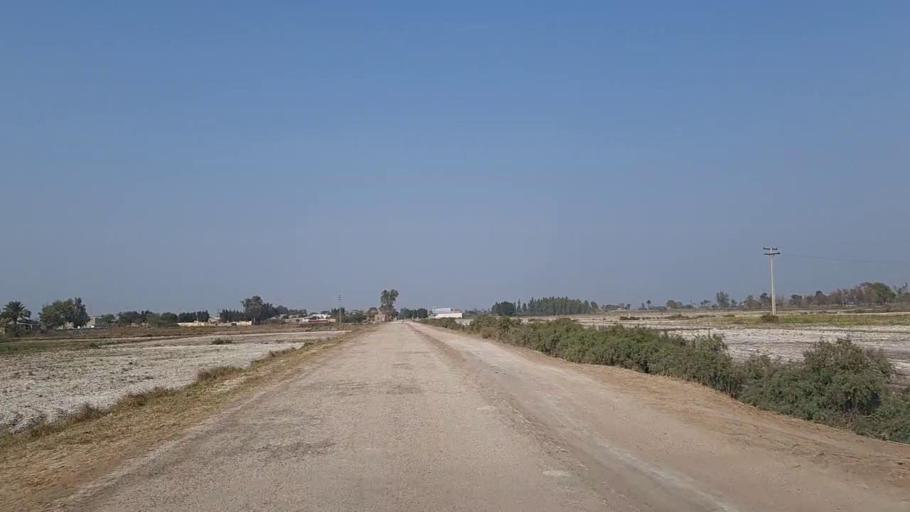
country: PK
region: Sindh
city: Daur
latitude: 26.4228
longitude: 68.4089
